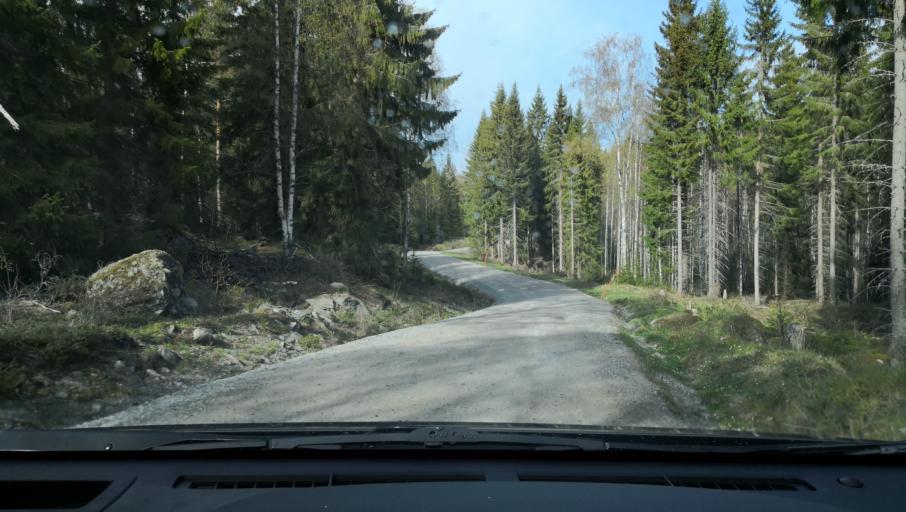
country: SE
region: Vaestmanland
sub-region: Fagersta Kommun
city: Fagersta
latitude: 60.1571
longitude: 15.6974
